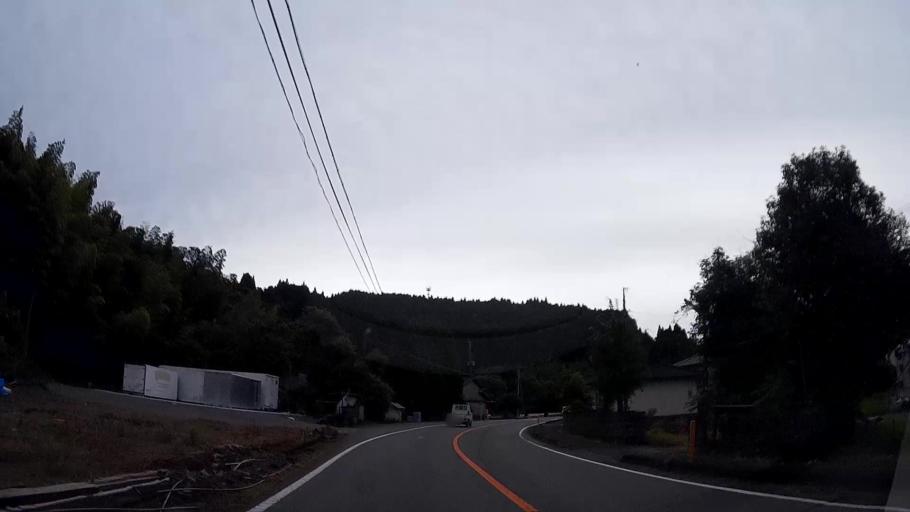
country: JP
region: Kumamoto
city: Kikuchi
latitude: 33.0164
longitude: 130.8777
